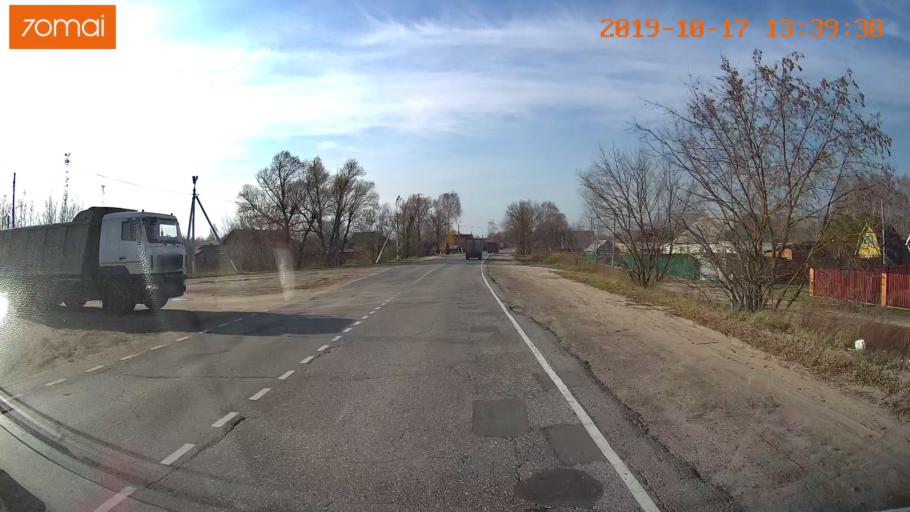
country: RU
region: Rjazan
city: Tuma
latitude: 55.1462
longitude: 40.5839
